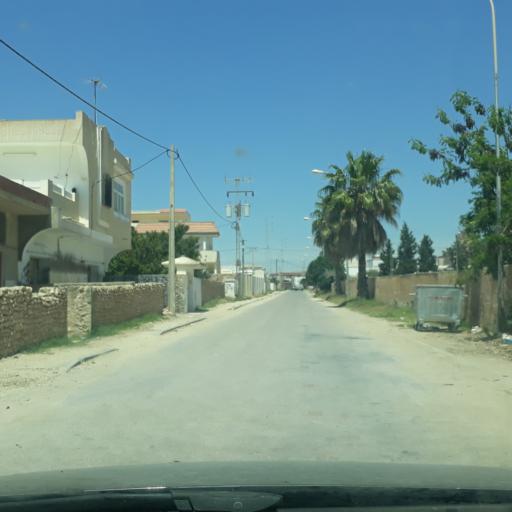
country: TN
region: Safaqis
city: Al Qarmadah
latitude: 34.8131
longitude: 10.7586
